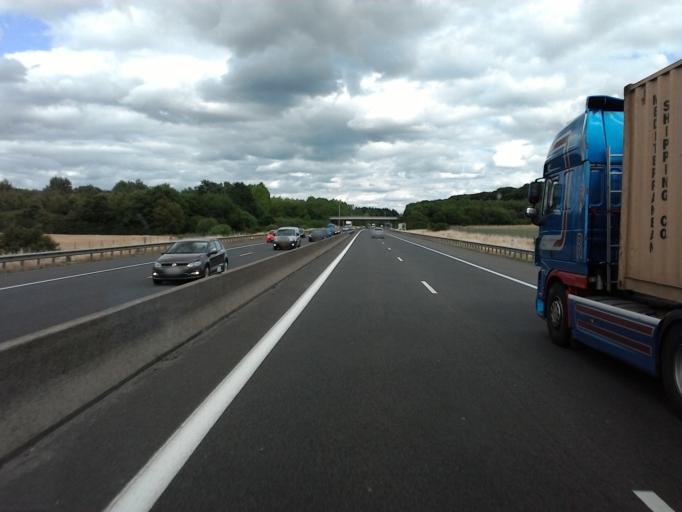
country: LU
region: Luxembourg
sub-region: Canton de Capellen
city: Garnich
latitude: 49.6360
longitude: 5.9370
